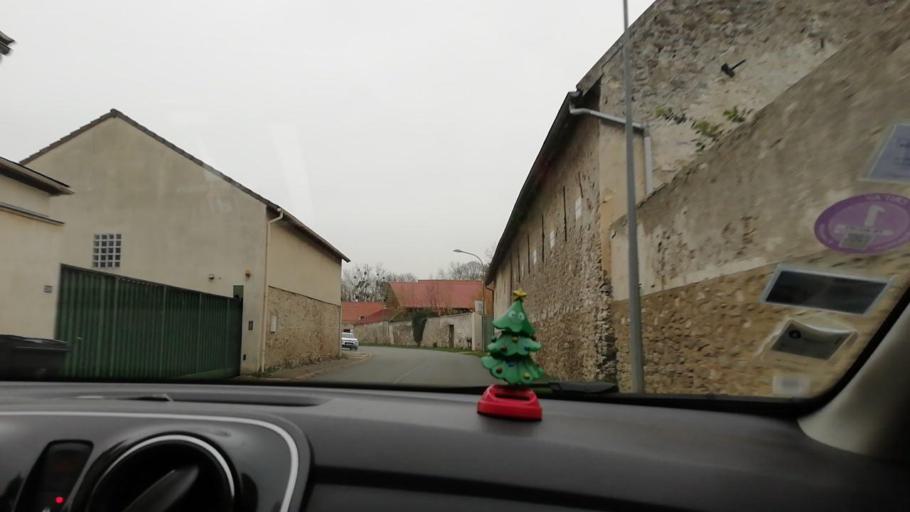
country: FR
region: Ile-de-France
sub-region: Departement de Seine-et-Marne
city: Charny
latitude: 48.9809
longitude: 2.7844
